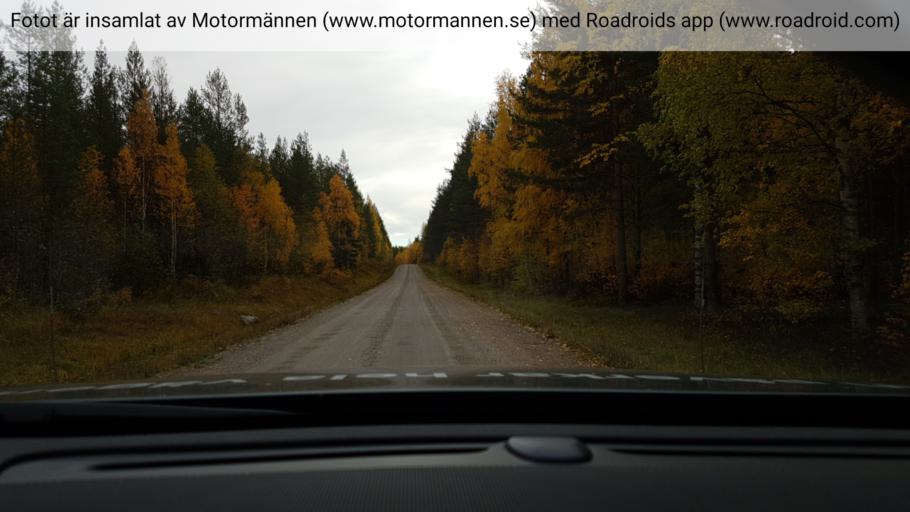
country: SE
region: Norrbotten
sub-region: Overkalix Kommun
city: OEverkalix
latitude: 66.2770
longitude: 22.9835
